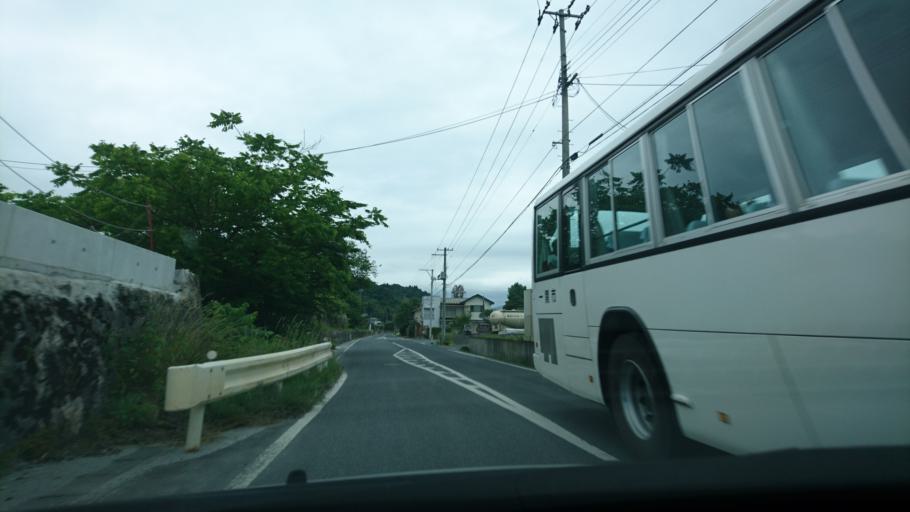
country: JP
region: Iwate
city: Ichinoseki
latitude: 38.9773
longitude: 141.2391
